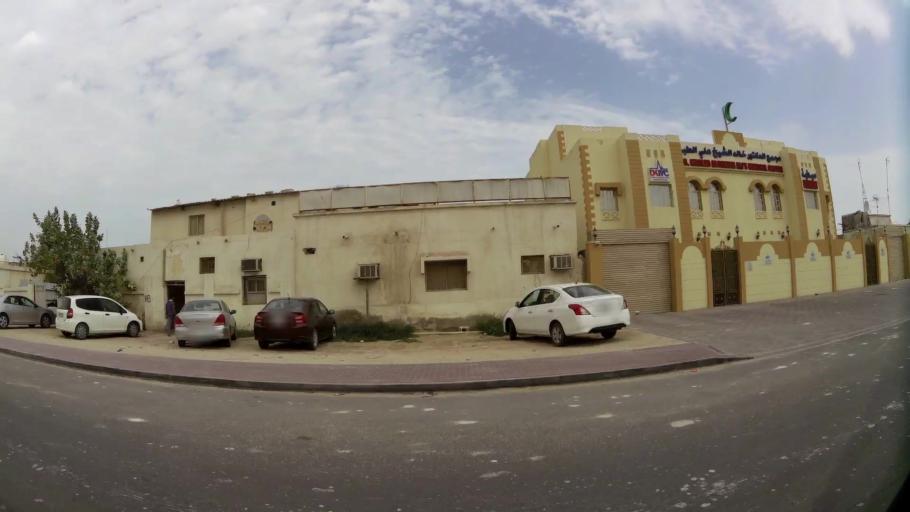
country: QA
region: Baladiyat ar Rayyan
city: Ar Rayyan
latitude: 25.3248
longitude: 51.4700
